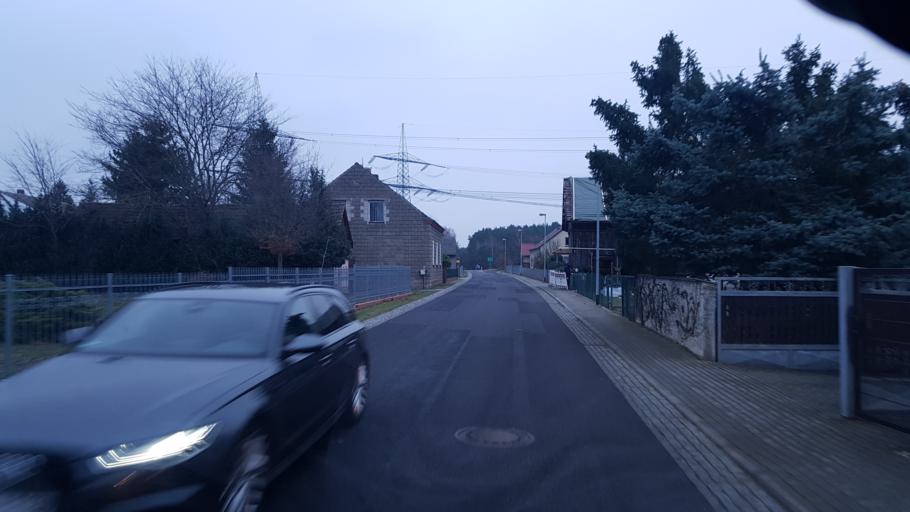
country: DE
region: Brandenburg
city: Guhrow
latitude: 51.8520
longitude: 14.2226
